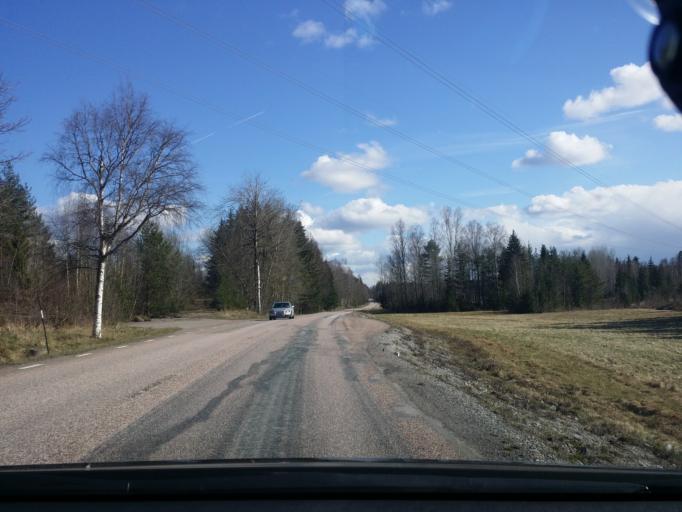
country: SE
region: Vaestmanland
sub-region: Sala Kommun
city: Sala
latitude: 59.9814
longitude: 16.4883
